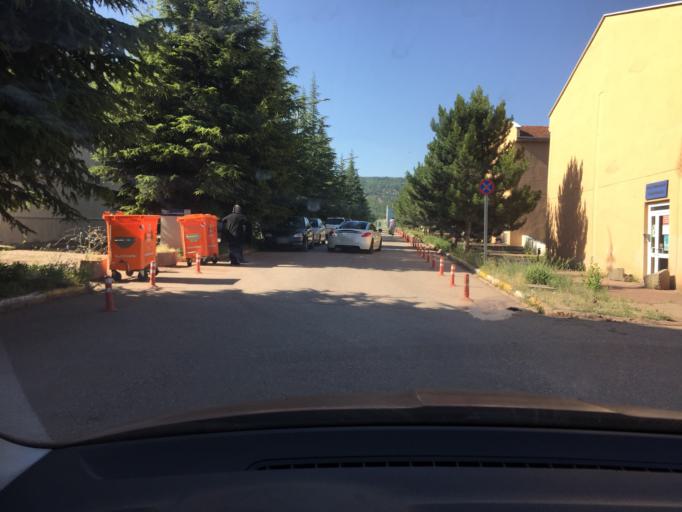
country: TR
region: Eskisehir
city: Eskisehir
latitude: 39.7487
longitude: 30.4749
